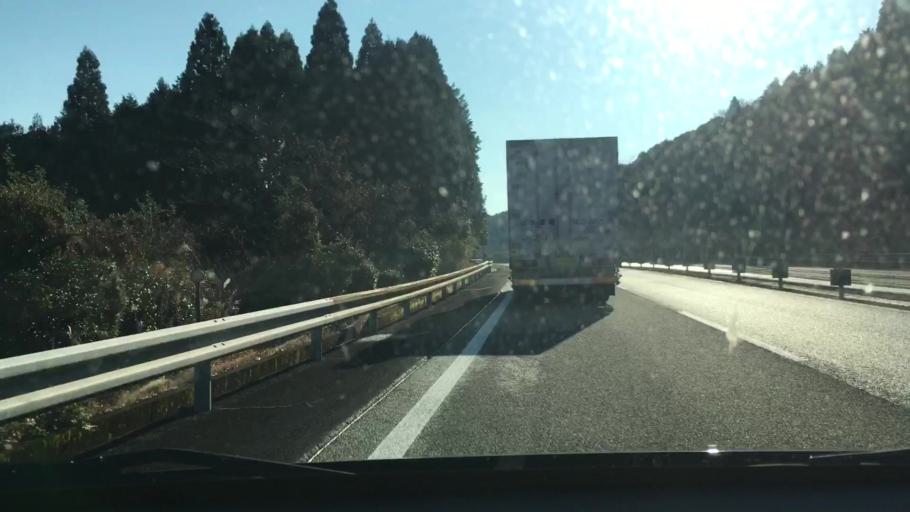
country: JP
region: Kagoshima
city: Kajiki
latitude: 31.8917
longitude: 130.6986
